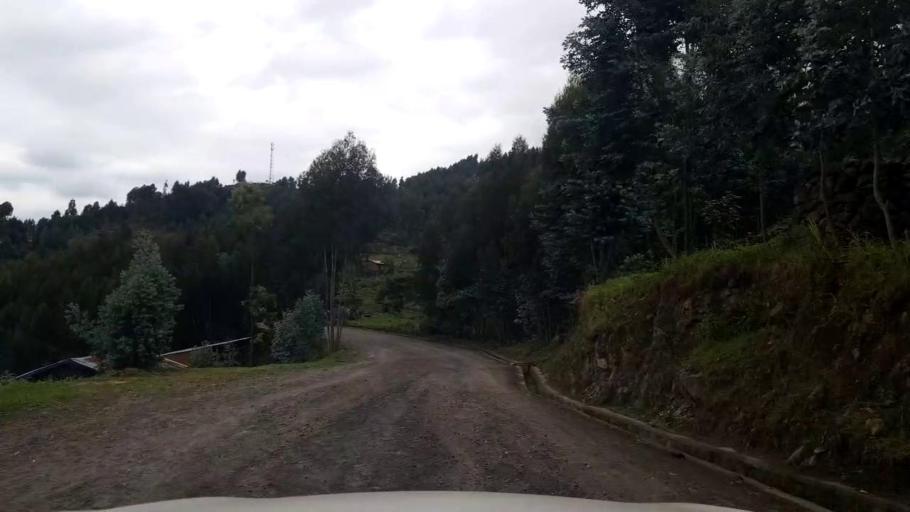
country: RW
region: Northern Province
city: Musanze
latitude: -1.5176
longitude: 29.5343
